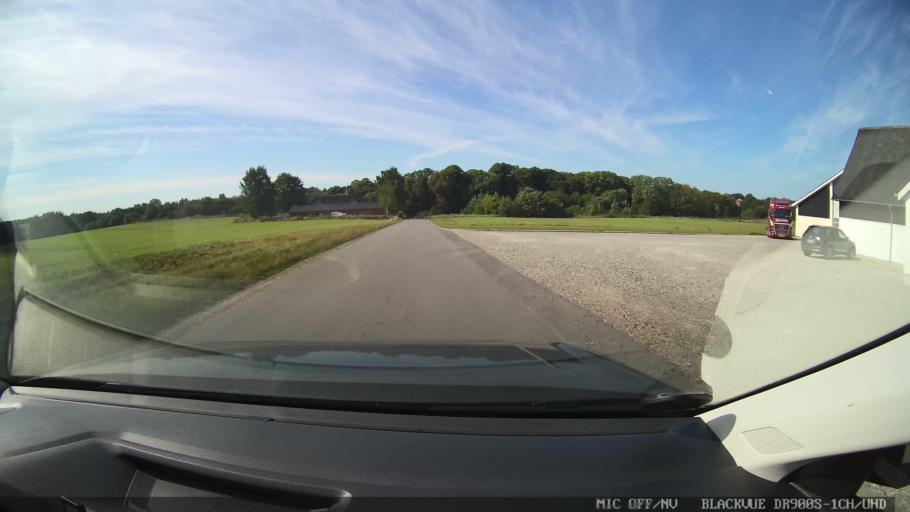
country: DK
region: North Denmark
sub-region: Mariagerfjord Kommune
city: Hobro
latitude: 56.5291
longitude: 9.7349
